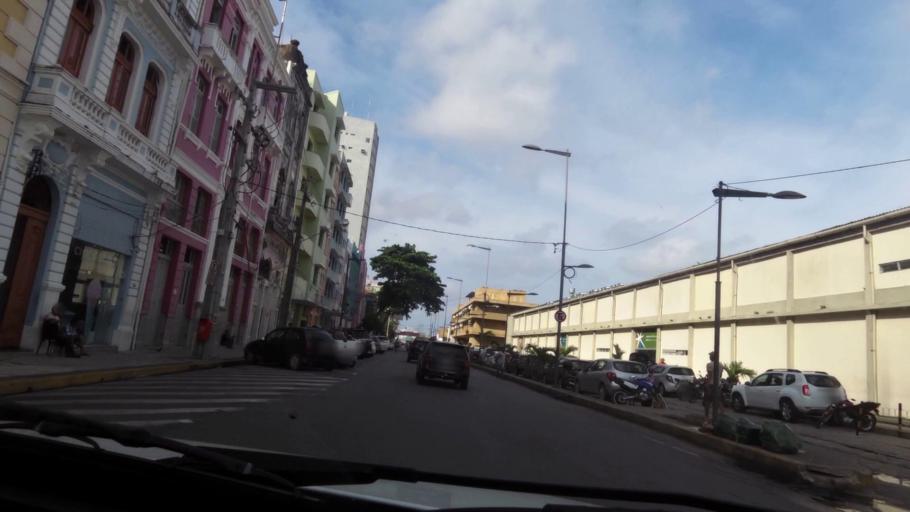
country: BR
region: Pernambuco
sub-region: Recife
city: Recife
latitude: -8.0605
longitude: -34.8703
